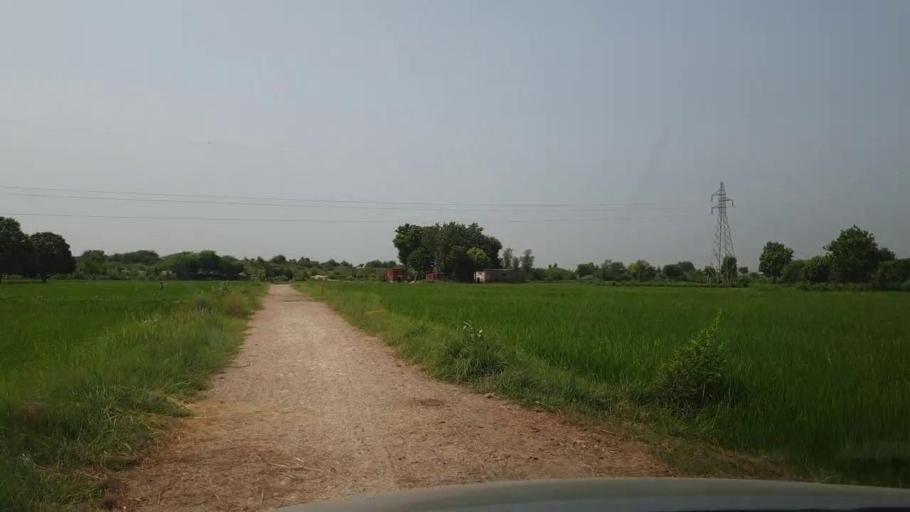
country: PK
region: Sindh
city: Madeji
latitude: 27.7870
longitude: 68.5372
